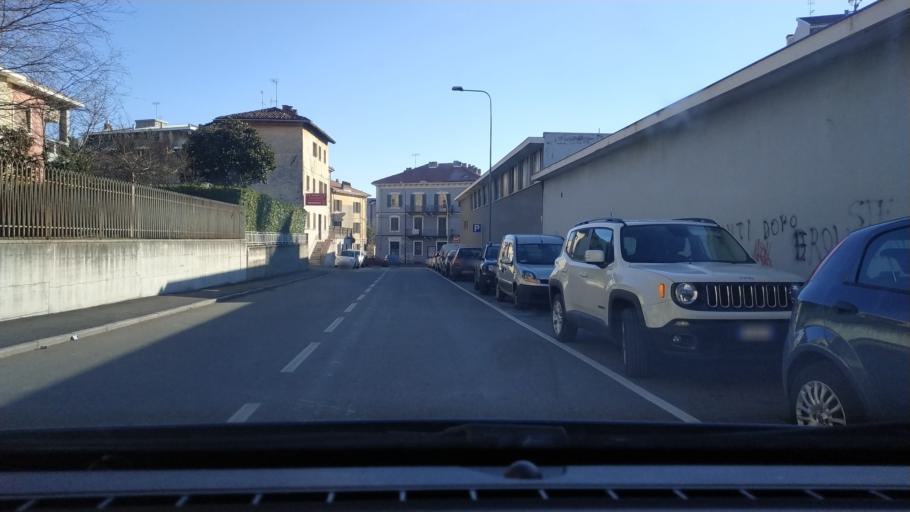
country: IT
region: Piedmont
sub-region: Provincia di Torino
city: Ivrea
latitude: 45.4690
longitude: 7.8886
